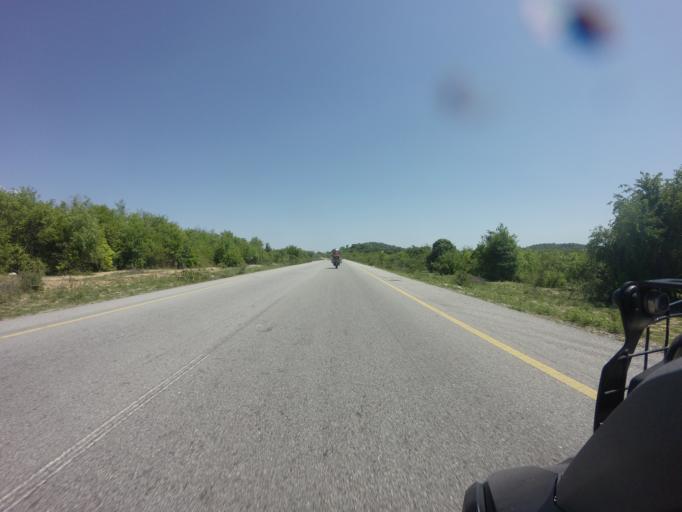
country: AO
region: Benguela
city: Benguela
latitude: -13.3012
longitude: 13.8091
